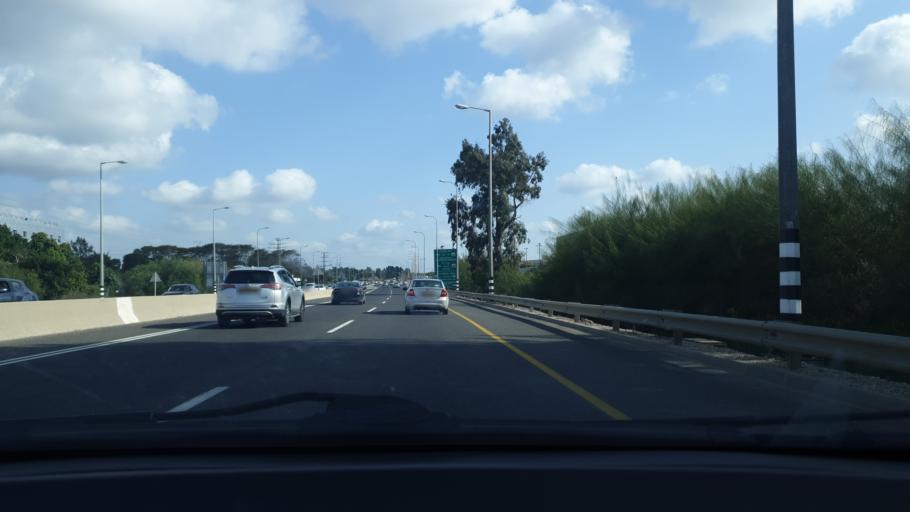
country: IL
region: Central District
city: Kefar Habad
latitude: 31.9625
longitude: 34.8493
